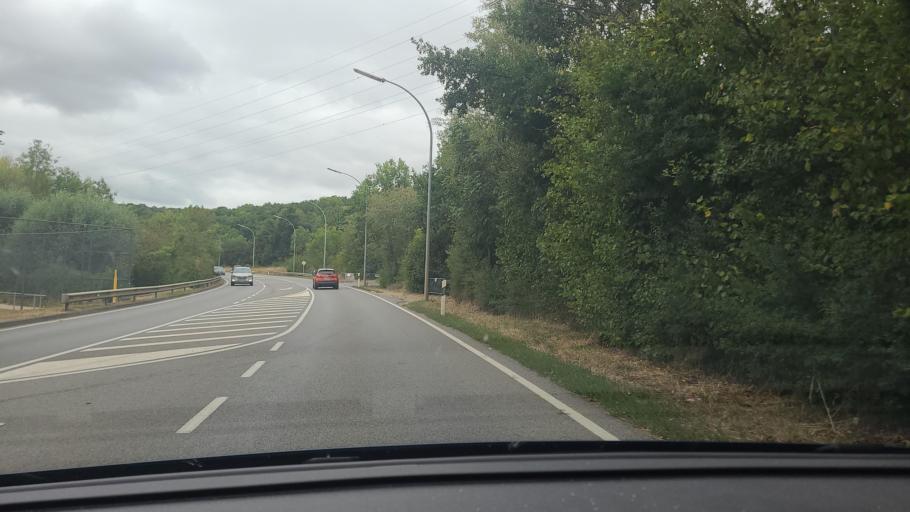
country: LU
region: Luxembourg
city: Lamadelaine
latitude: 49.5570
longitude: 5.8586
